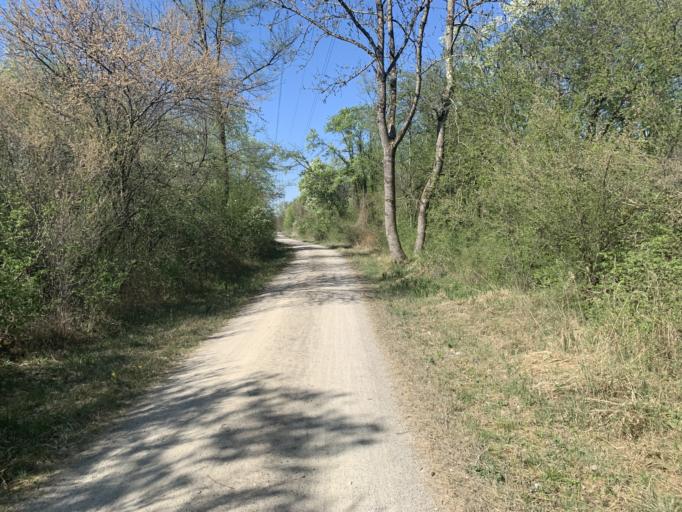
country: DE
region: Bavaria
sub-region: Swabia
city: Gersthofen
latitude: 48.4556
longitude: 10.8862
